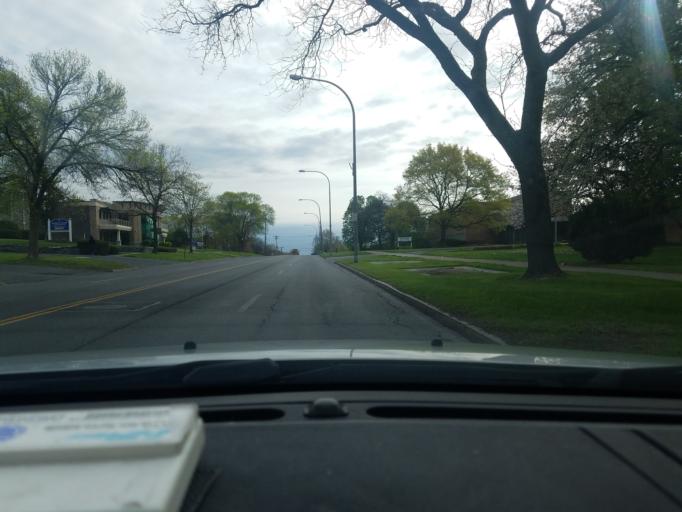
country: US
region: New York
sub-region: Onondaga County
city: Syracuse
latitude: 43.0596
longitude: -76.1338
